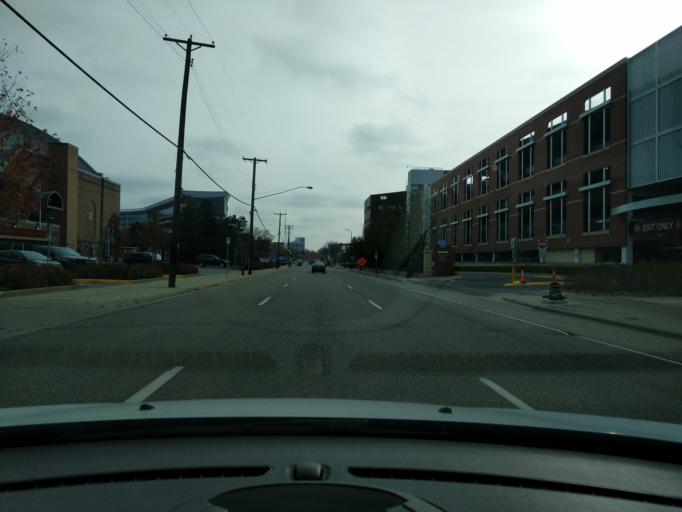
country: US
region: Minnesota
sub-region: Ramsey County
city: Lauderdale
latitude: 44.9766
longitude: -93.2292
